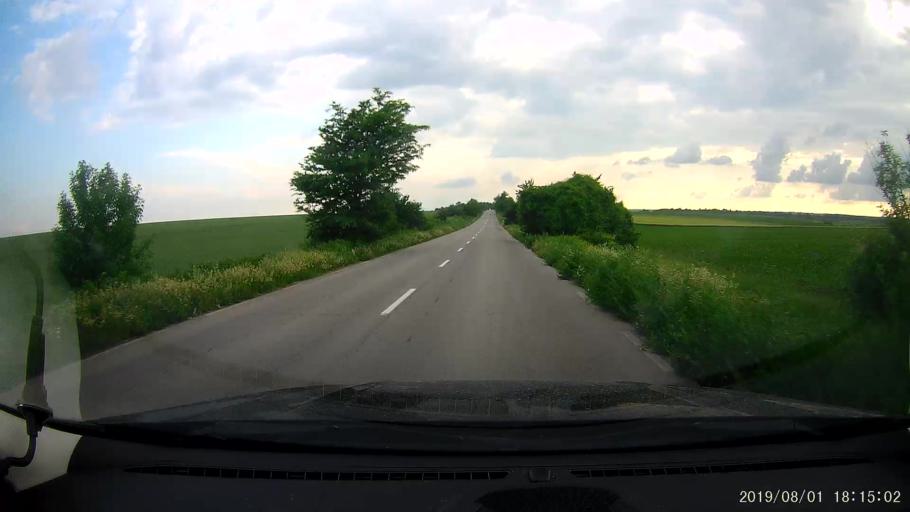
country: BG
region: Silistra
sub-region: Obshtina Dulovo
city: Dulovo
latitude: 43.7598
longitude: 27.1134
